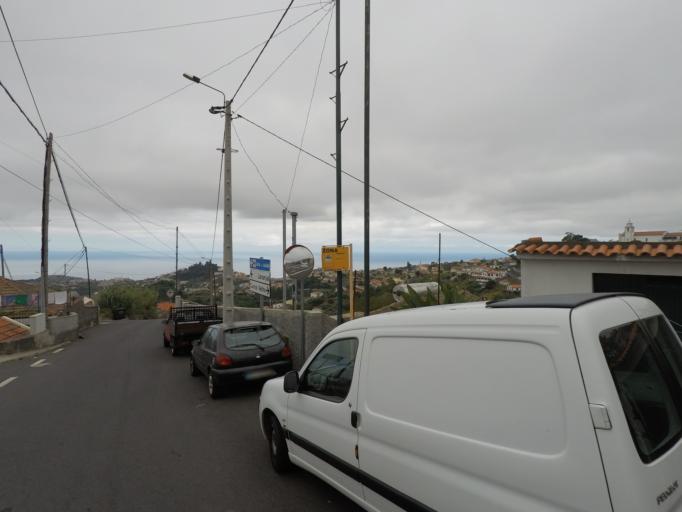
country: PT
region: Madeira
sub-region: Funchal
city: Nossa Senhora do Monte
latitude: 32.6780
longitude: -16.9430
